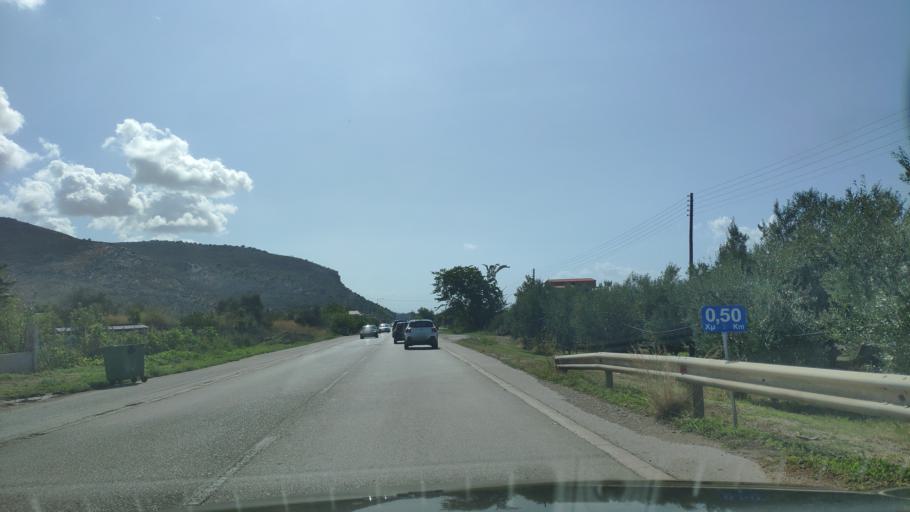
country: GR
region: West Greece
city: Aitoliko
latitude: 38.4689
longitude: 21.3589
